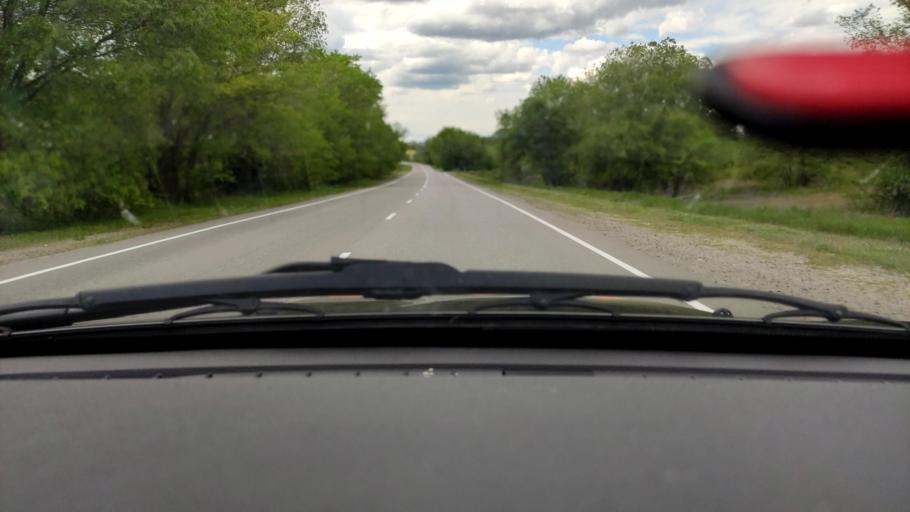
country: RU
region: Voronezj
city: Ostrogozhsk
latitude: 51.0546
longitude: 38.9271
